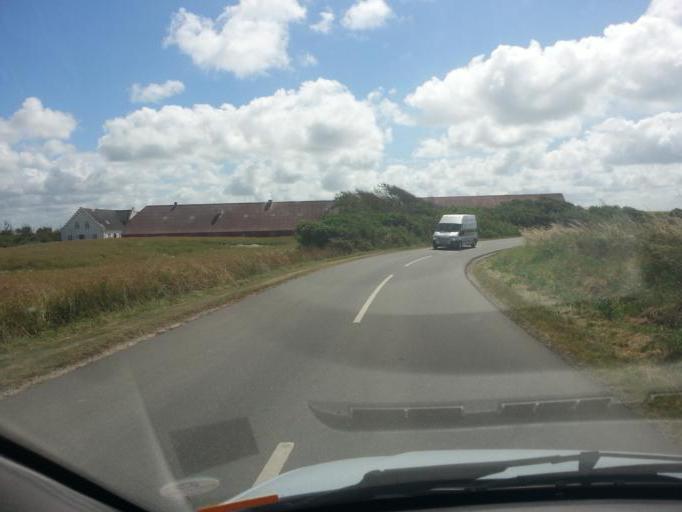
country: DK
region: Central Jutland
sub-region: Lemvig Kommune
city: Harboore
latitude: 56.5039
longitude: 8.1414
